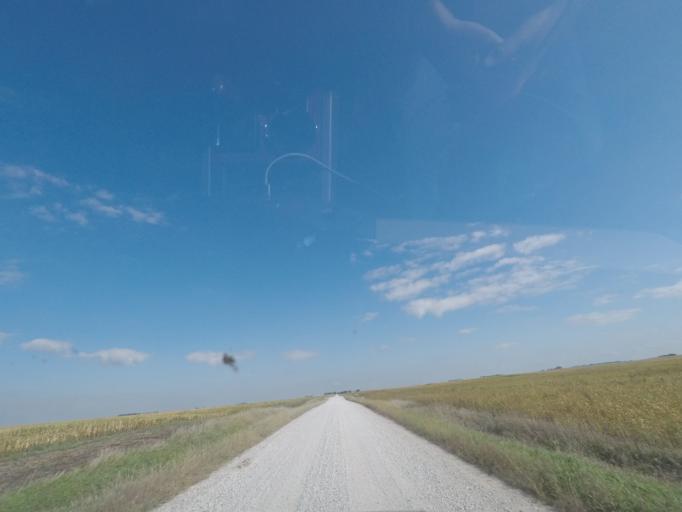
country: US
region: Iowa
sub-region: Story County
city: Nevada
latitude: 42.0396
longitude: -93.4252
